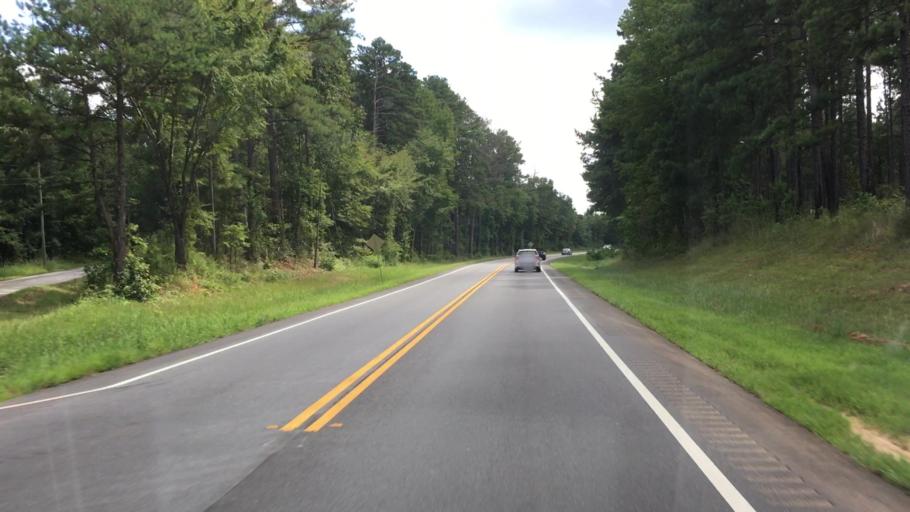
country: US
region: Georgia
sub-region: Putnam County
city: Eatonton
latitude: 33.3969
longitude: -83.3688
